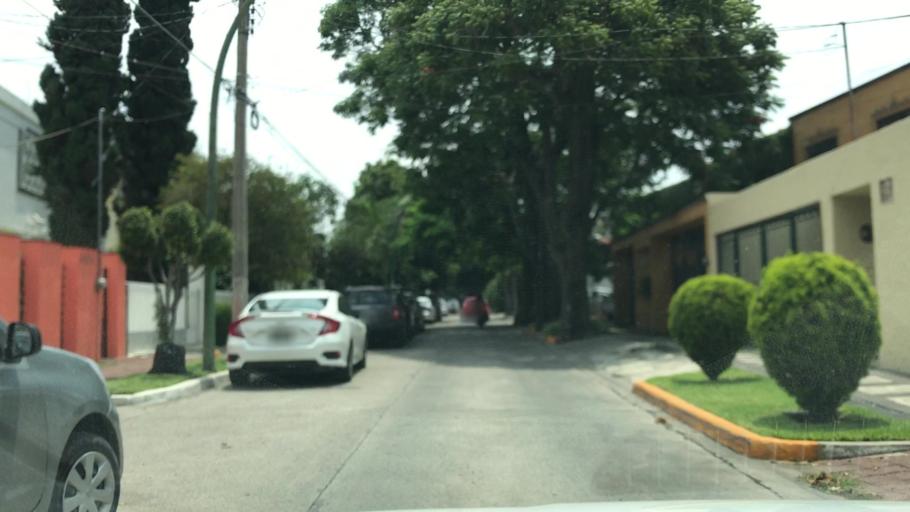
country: MX
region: Jalisco
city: Guadalajara
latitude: 20.6647
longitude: -103.4070
